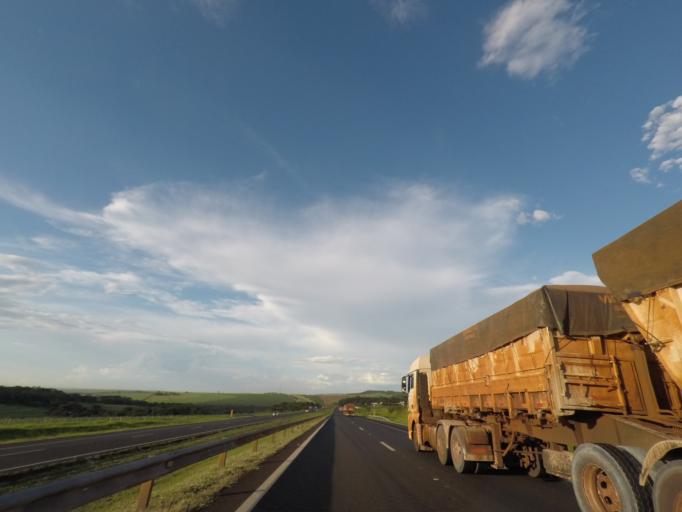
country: BR
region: Sao Paulo
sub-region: Ituverava
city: Ituverava
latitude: -20.2993
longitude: -47.7993
